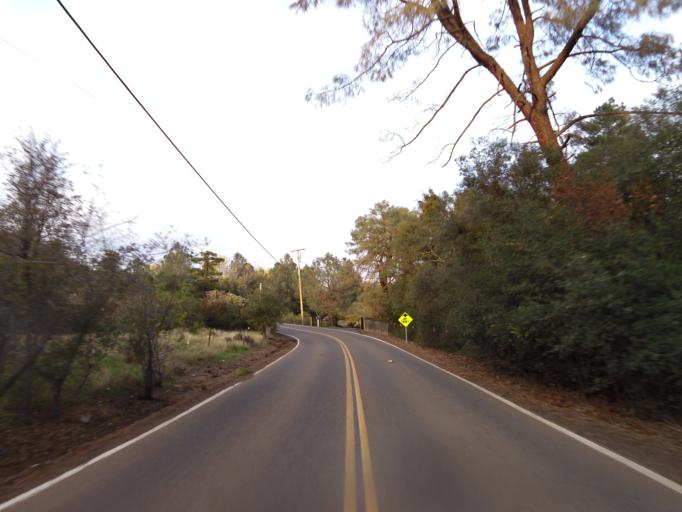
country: US
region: California
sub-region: El Dorado County
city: Cameron Park
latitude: 38.7228
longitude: -121.0040
